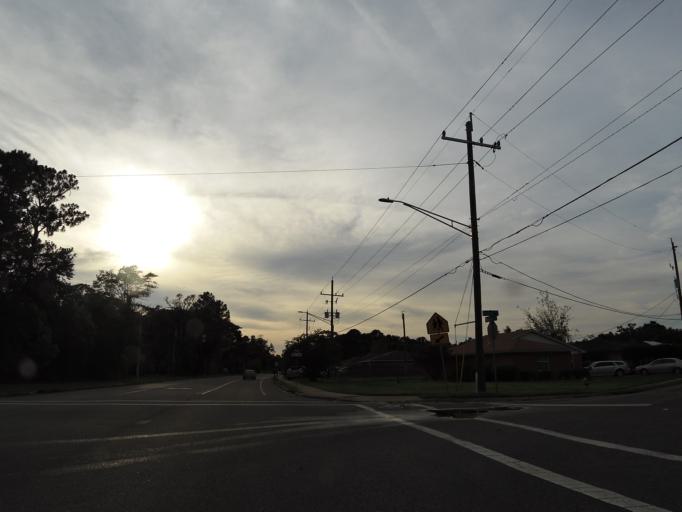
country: US
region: Florida
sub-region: Duval County
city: Jacksonville
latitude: 30.3920
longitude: -81.7310
